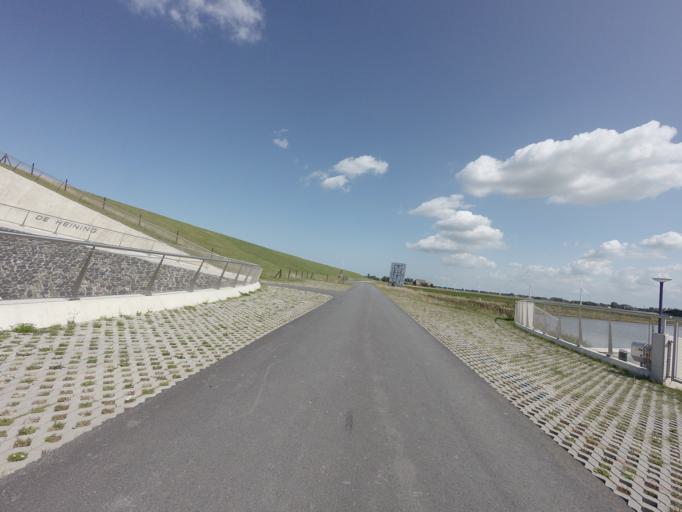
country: NL
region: Friesland
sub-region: Gemeente Ferwerderadiel
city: Hallum
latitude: 53.3213
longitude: 5.7593
